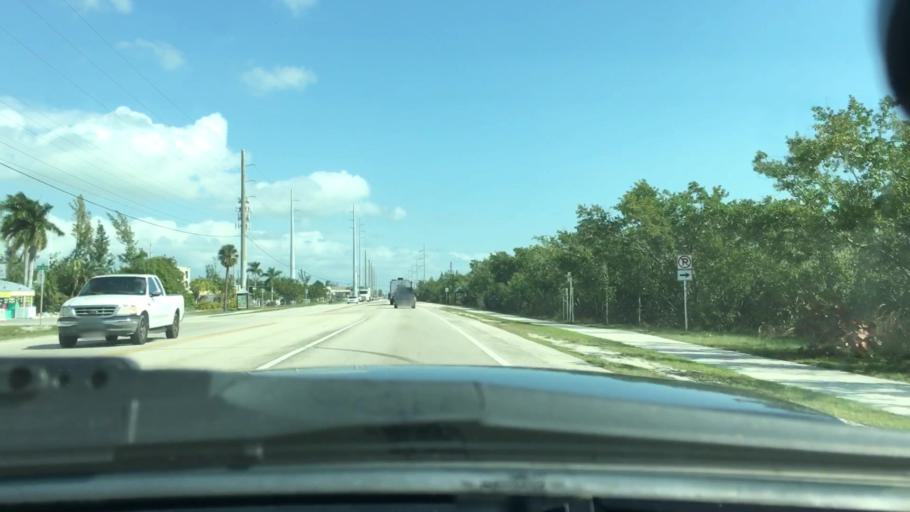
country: US
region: Florida
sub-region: Monroe County
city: Big Coppitt Key
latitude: 24.5944
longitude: -81.6626
